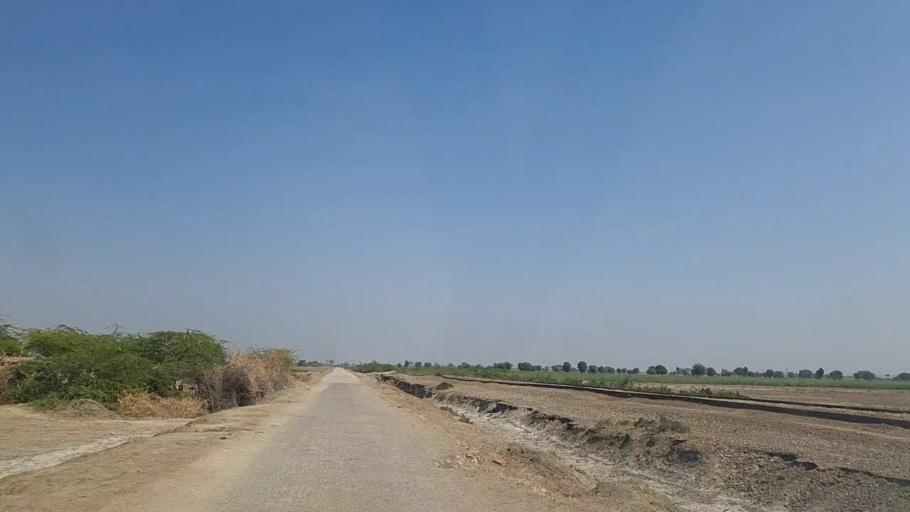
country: PK
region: Sindh
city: Naukot
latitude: 24.8699
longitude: 69.4215
